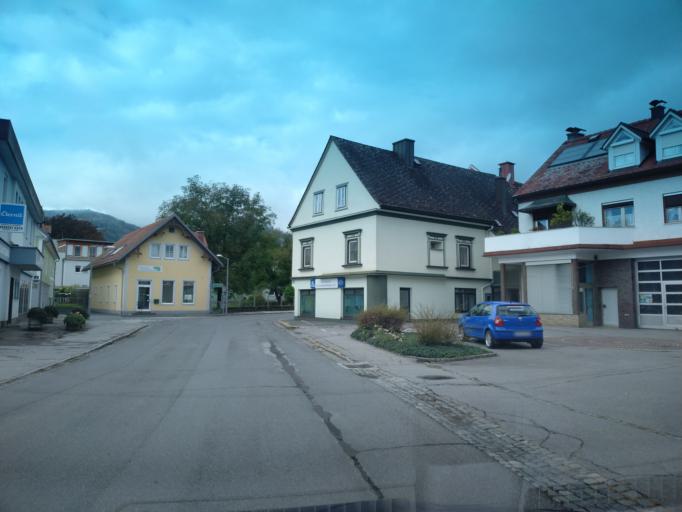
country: AT
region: Styria
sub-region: Politischer Bezirk Deutschlandsberg
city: Deutschlandsberg
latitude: 46.8152
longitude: 15.2177
